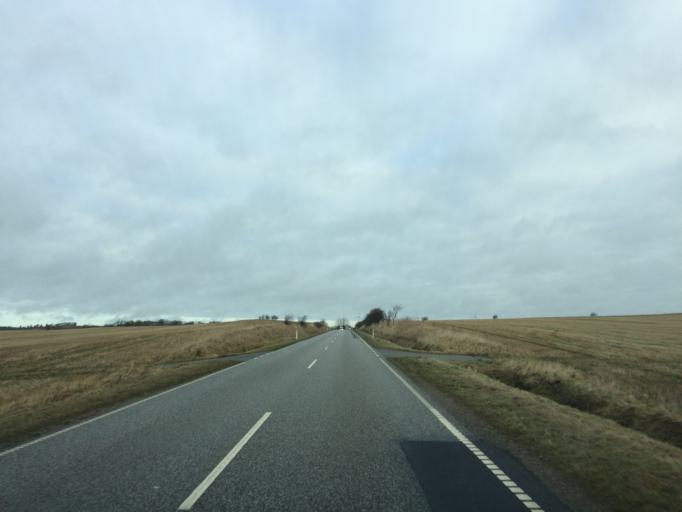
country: DK
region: Central Jutland
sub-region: Struer Kommune
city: Struer
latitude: 56.4115
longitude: 8.4792
